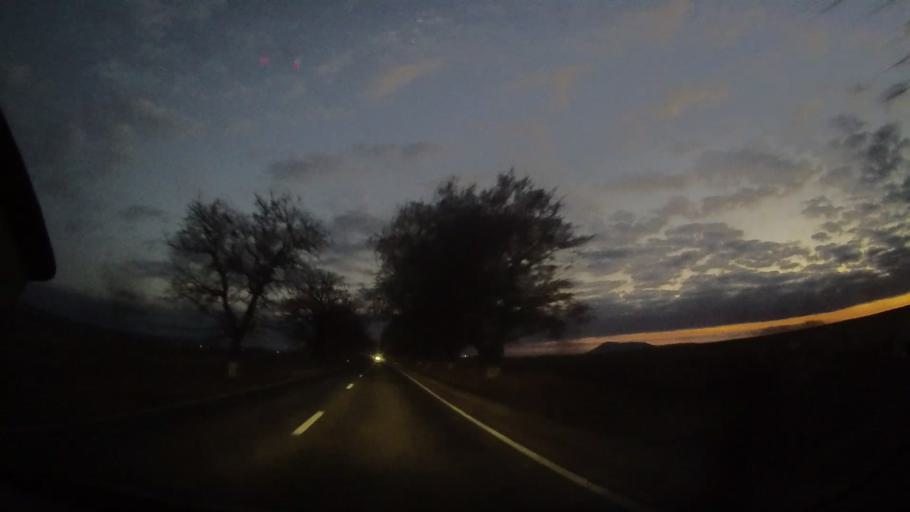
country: RO
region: Tulcea
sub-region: Comuna Mihail Kogalniceanu
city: Mihail Kogalniceanu
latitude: 45.0561
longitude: 28.7371
